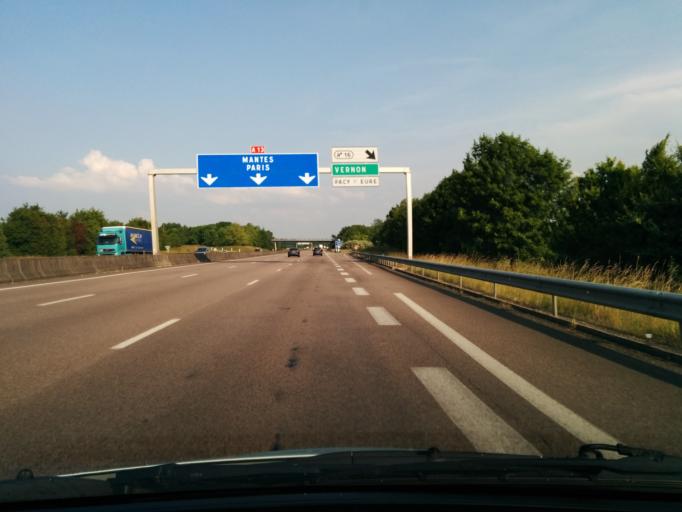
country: FR
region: Haute-Normandie
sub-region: Departement de l'Eure
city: Saint-Marcel
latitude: 49.0656
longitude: 1.4178
